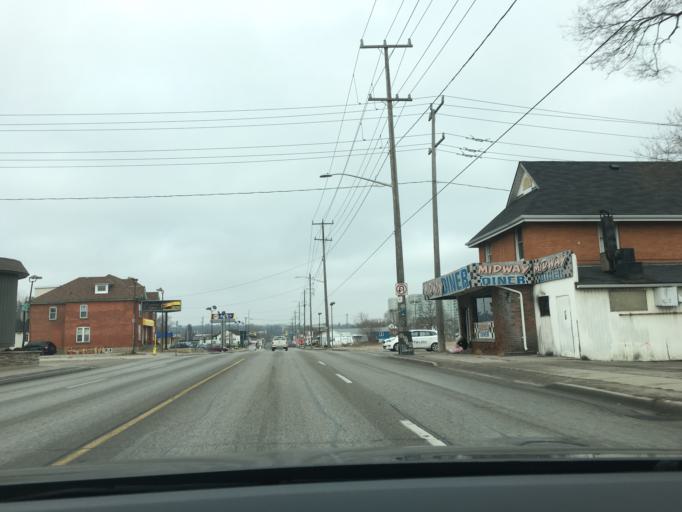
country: CA
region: Ontario
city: Barrie
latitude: 44.3793
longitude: -79.6936
